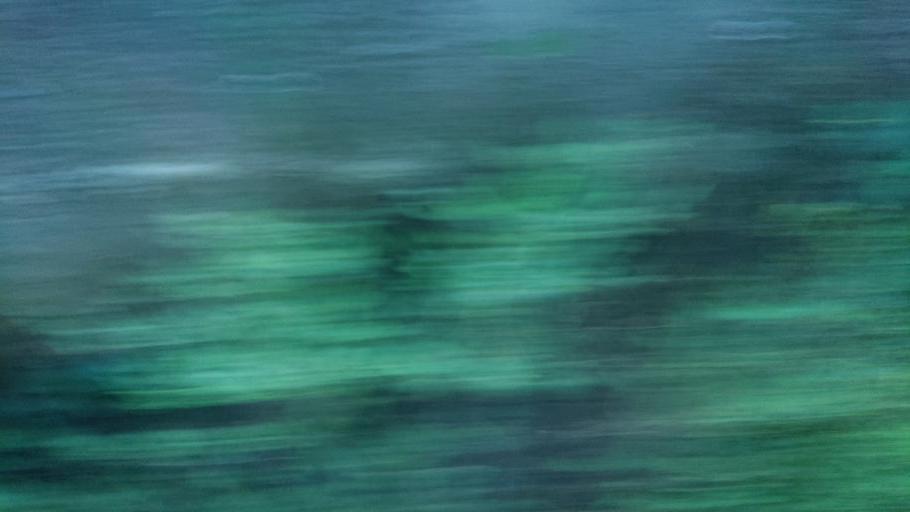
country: TW
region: Taiwan
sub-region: Chiayi
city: Jiayi Shi
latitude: 23.5251
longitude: 120.6324
